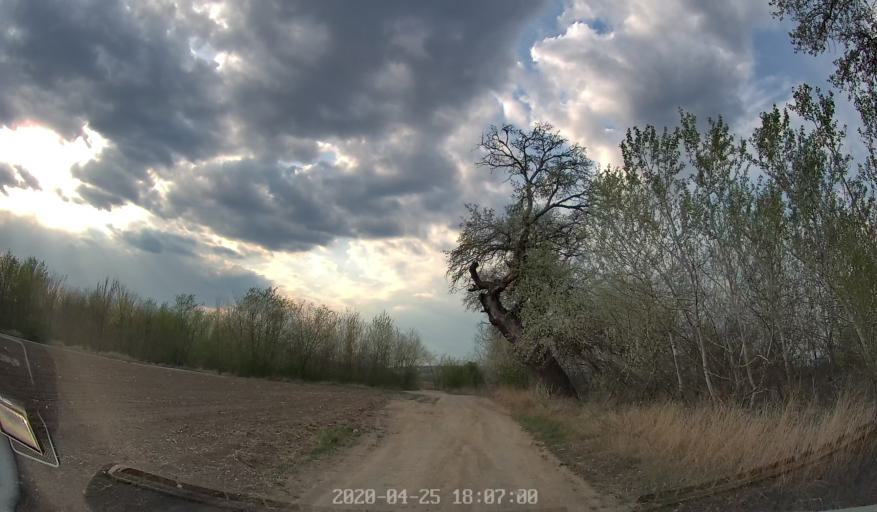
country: MD
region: Chisinau
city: Vadul lui Voda
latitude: 47.1285
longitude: 29.0836
